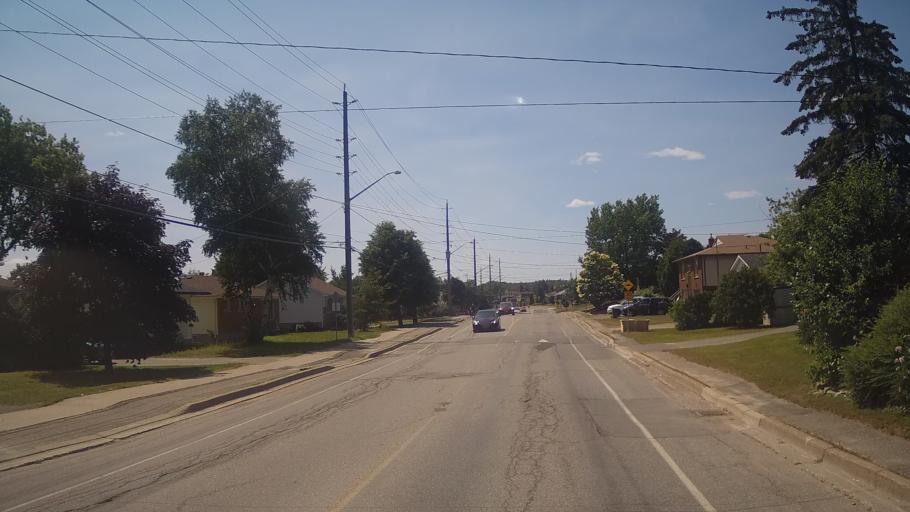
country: CA
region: Ontario
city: Greater Sudbury
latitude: 46.4597
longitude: -81.0230
